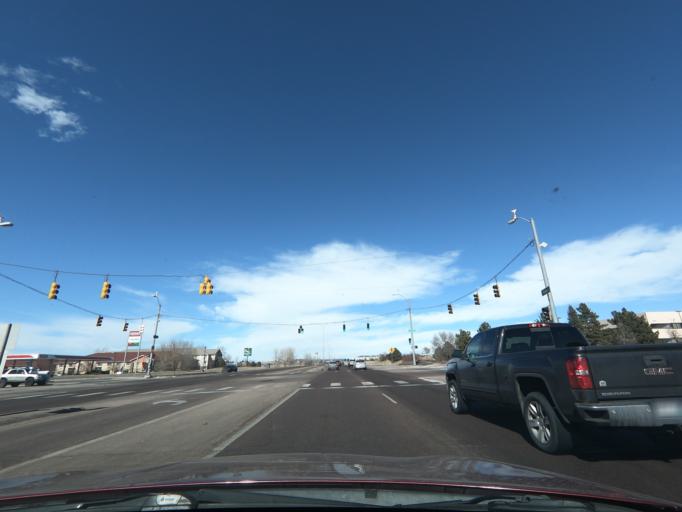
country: US
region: Colorado
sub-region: El Paso County
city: Security-Widefield
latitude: 38.7987
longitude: -104.7302
